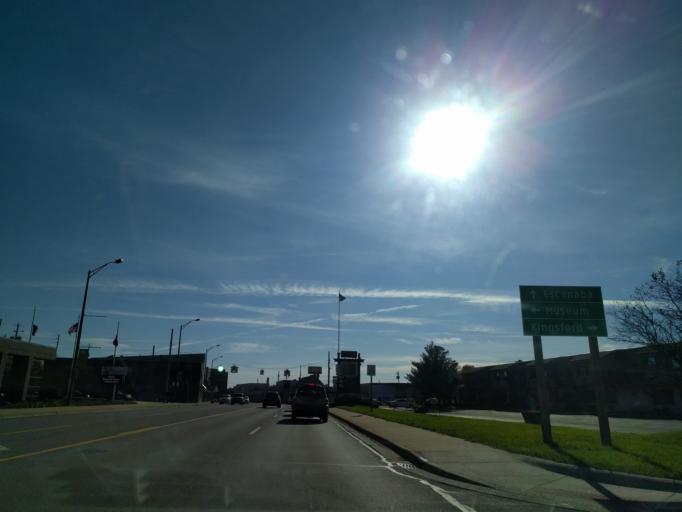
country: US
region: Michigan
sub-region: Dickinson County
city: Iron Mountain
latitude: 45.8212
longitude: -88.0652
